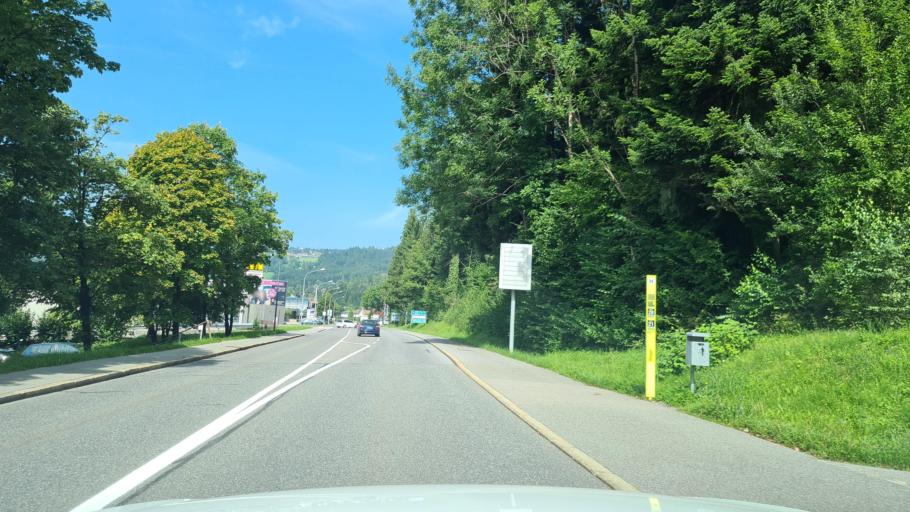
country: AT
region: Vorarlberg
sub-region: Politischer Bezirk Bregenz
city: Schwarzach
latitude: 47.4378
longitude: 9.7592
